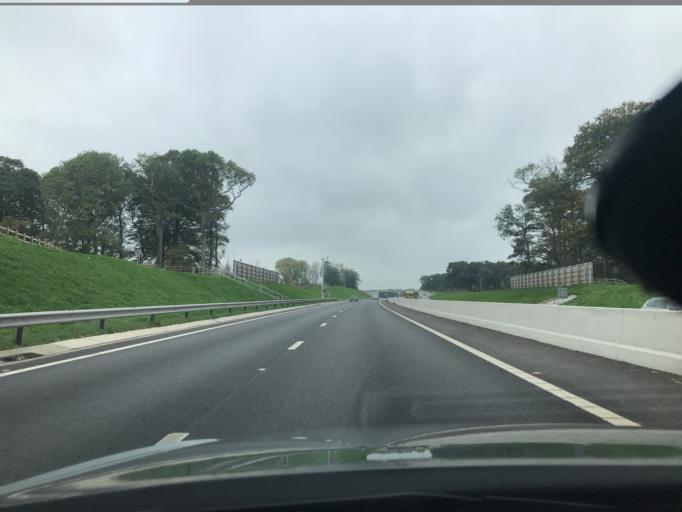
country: GB
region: England
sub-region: Cheshire East
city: Mere
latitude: 53.3366
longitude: -2.4176
